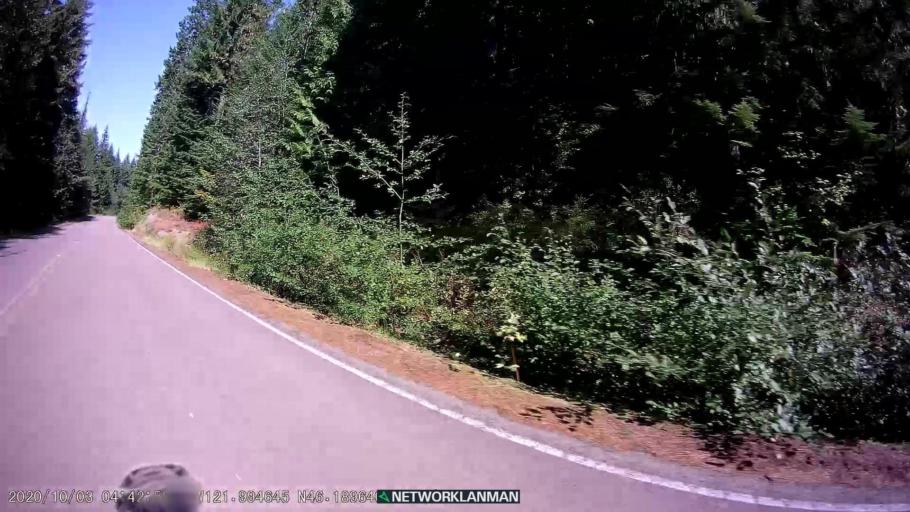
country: US
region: Washington
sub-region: Lewis County
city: Morton
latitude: 46.1899
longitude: -121.9946
